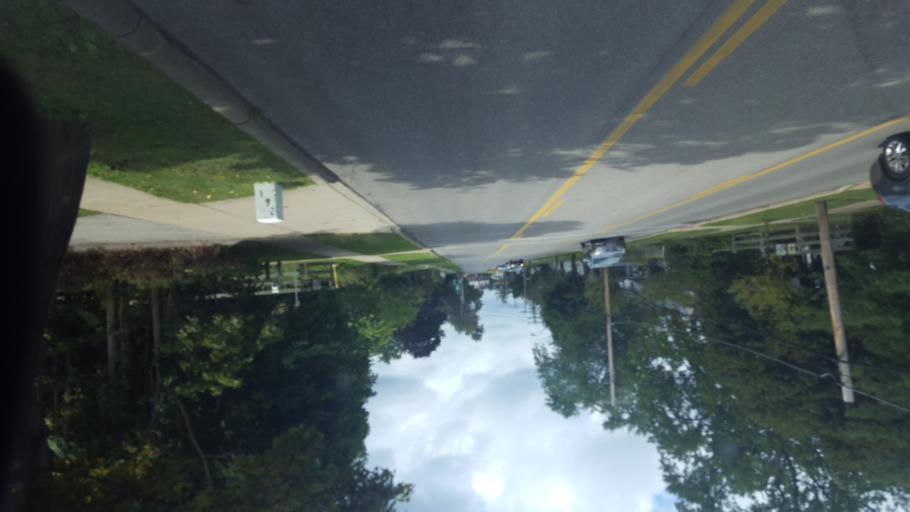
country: US
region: Ohio
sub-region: Lake County
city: Painesville
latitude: 41.7207
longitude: -81.2506
